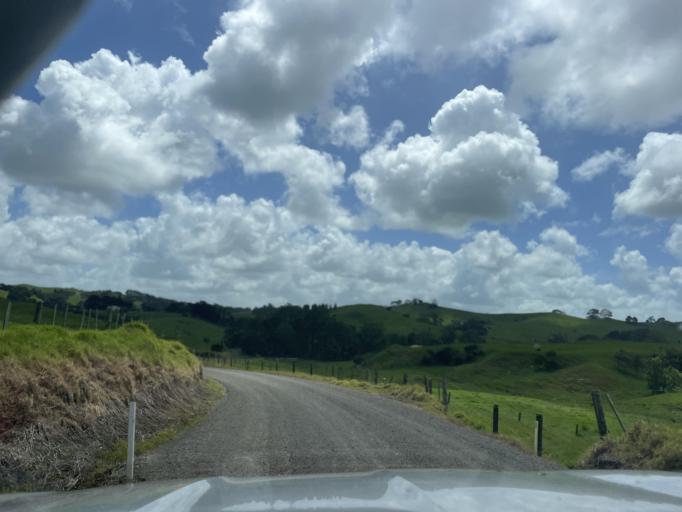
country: NZ
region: Auckland
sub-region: Auckland
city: Wellsford
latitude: -36.1942
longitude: 174.3346
